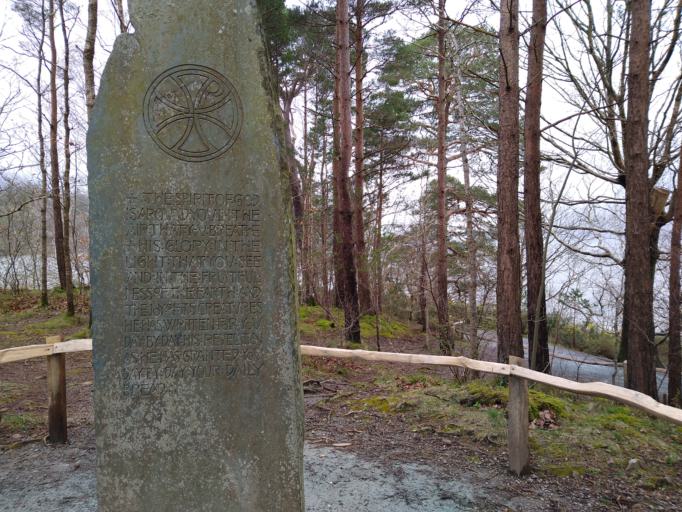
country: GB
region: England
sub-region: Cumbria
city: Keswick
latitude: 54.5904
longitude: -3.1408
